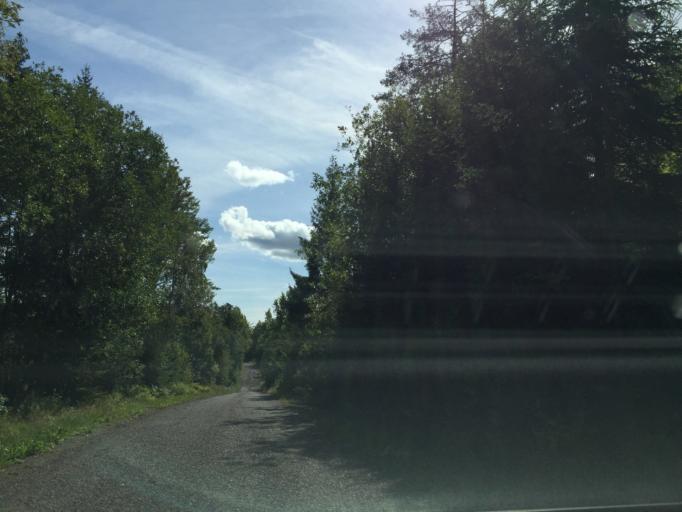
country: NO
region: Vestfold
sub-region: Hof
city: Hof
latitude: 59.4447
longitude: 10.1572
